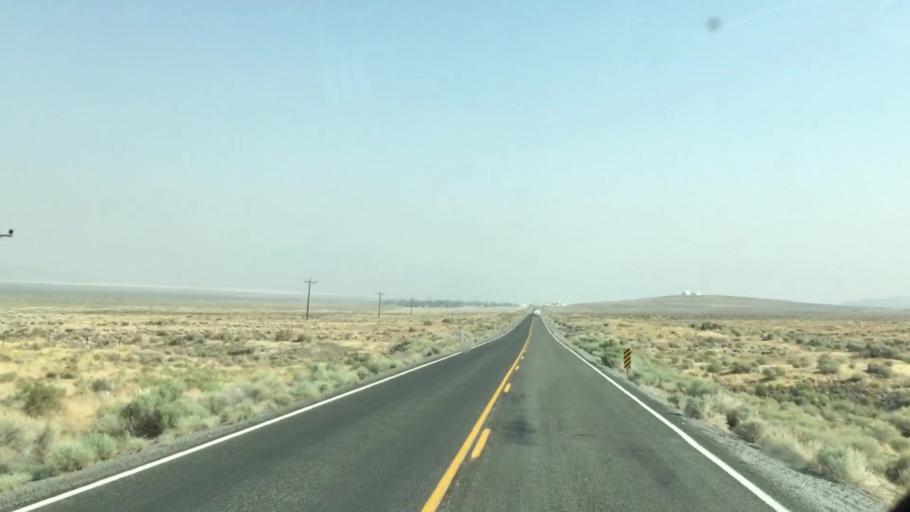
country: US
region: Nevada
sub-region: Pershing County
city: Lovelock
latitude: 40.5503
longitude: -119.3387
